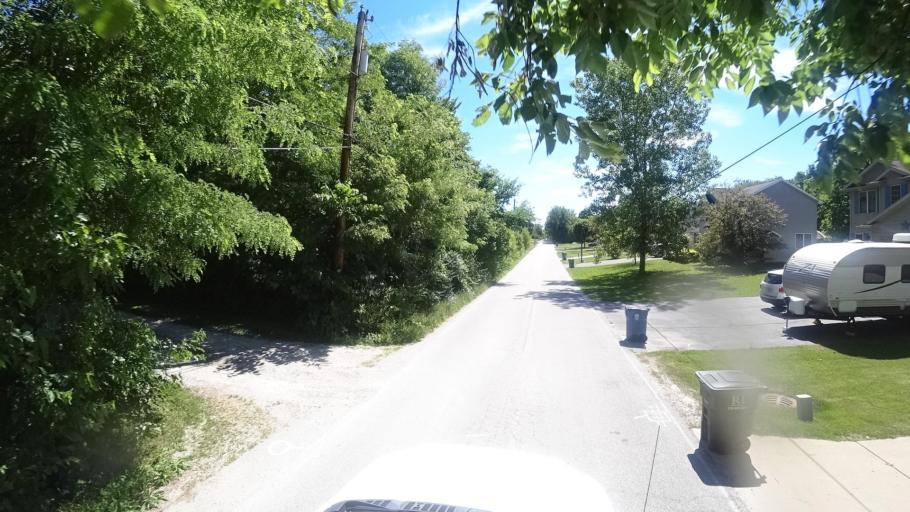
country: US
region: Indiana
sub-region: Porter County
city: Porter
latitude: 41.6296
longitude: -87.0767
